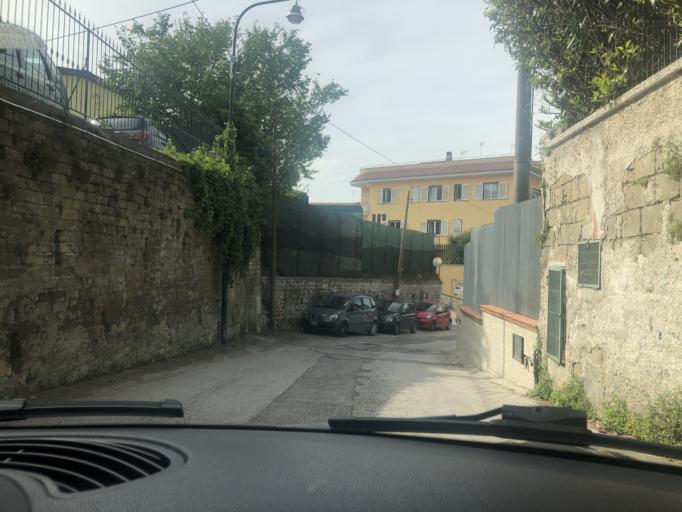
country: IT
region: Campania
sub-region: Provincia di Napoli
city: Torre Caracciolo
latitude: 40.8691
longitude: 14.1935
